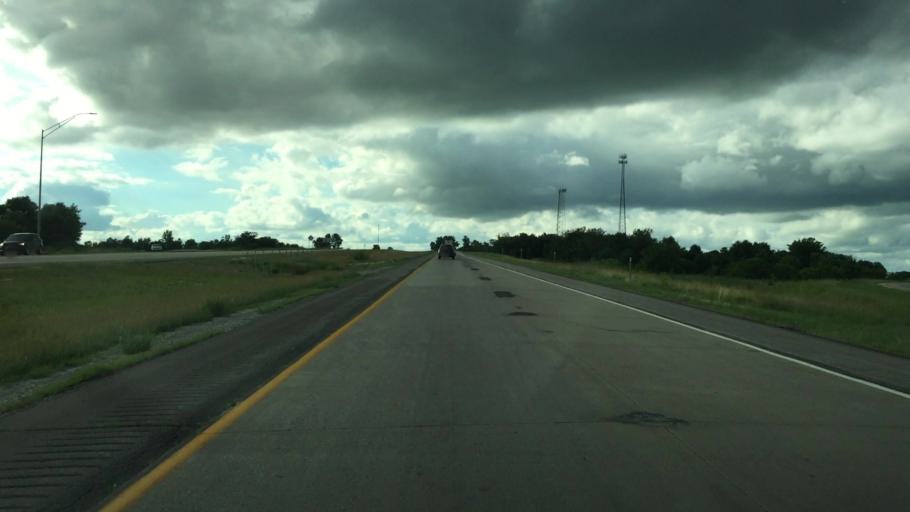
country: US
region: Iowa
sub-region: Polk County
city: Altoona
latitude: 41.6565
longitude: -93.5189
